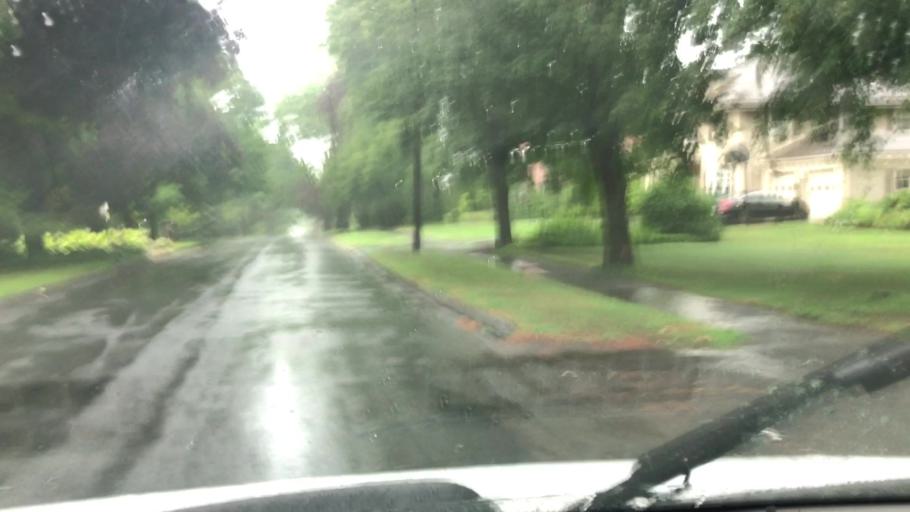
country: US
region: Massachusetts
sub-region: Berkshire County
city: Pittsfield
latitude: 42.4399
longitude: -73.2441
